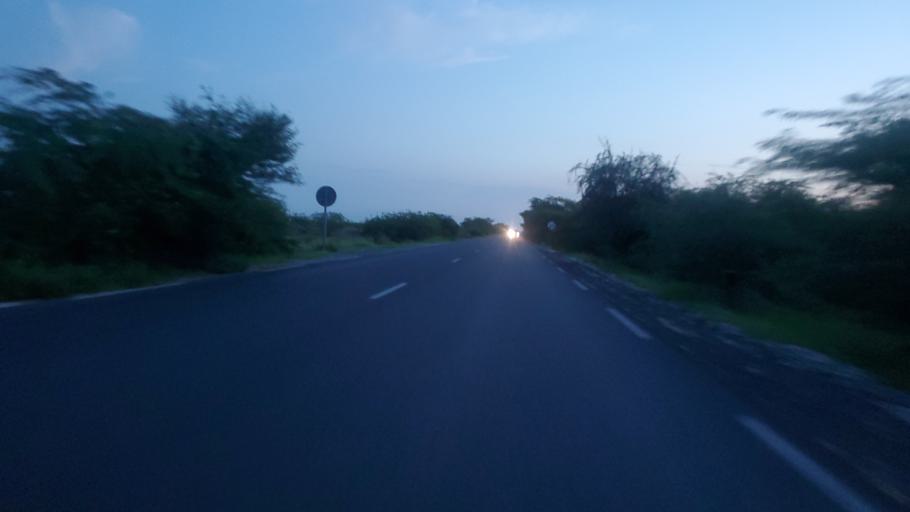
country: SN
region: Saint-Louis
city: Saint-Louis
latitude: 16.0636
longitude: -16.3944
